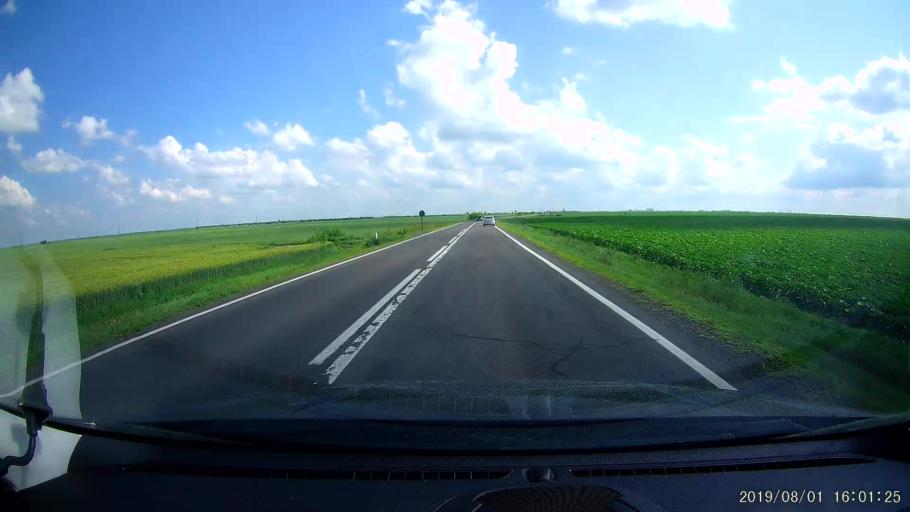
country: RO
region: Ialomita
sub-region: Comuna Ciulnita
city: Ciulnita
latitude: 44.5087
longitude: 27.3901
